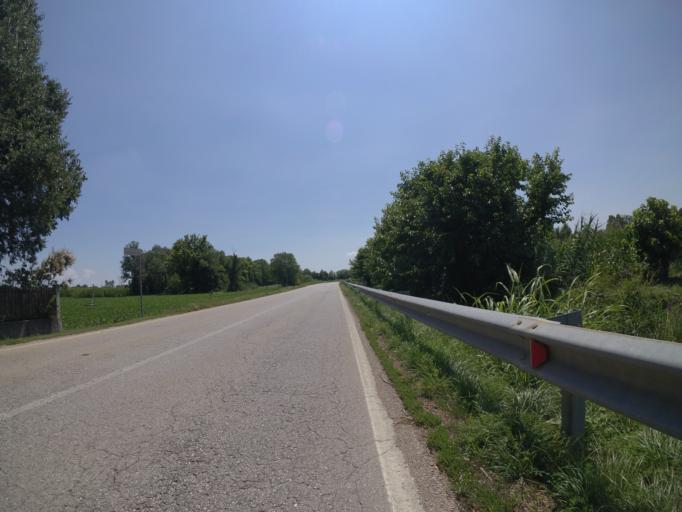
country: IT
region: Friuli Venezia Giulia
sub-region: Provincia di Udine
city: Lestizza
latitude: 45.9684
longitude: 13.1410
